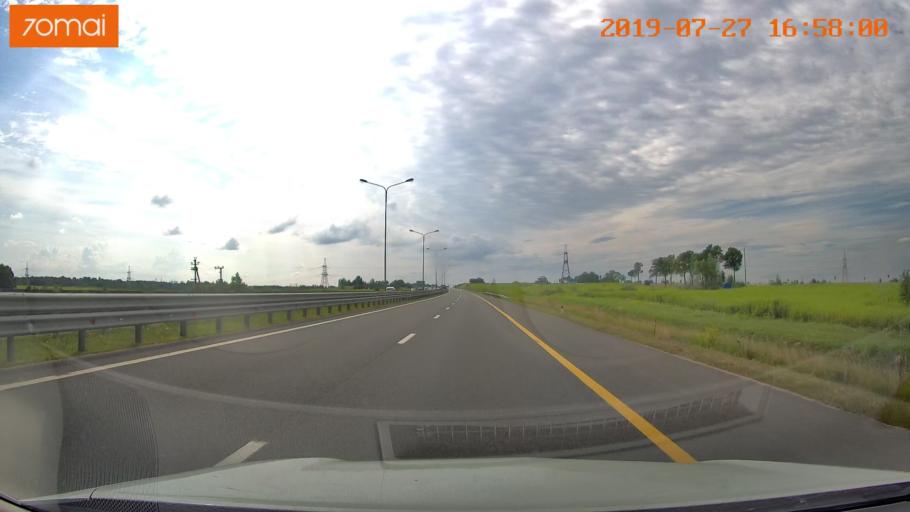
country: RU
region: Kaliningrad
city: Bol'shoe Isakovo
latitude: 54.7012
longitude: 20.6952
